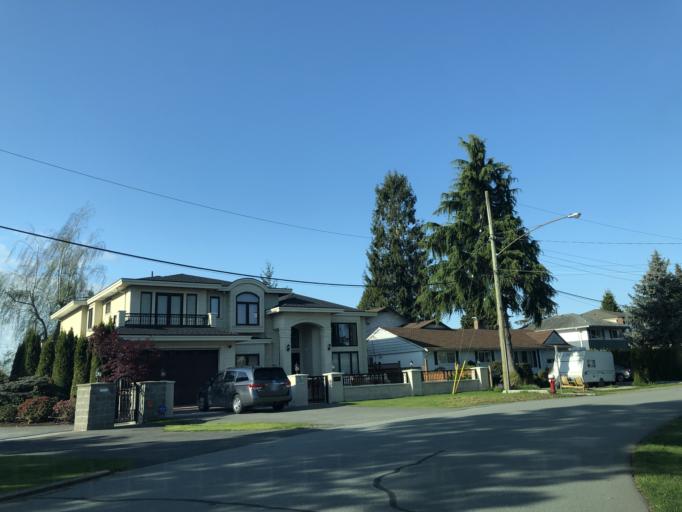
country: CA
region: British Columbia
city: Richmond
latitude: 49.1417
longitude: -123.1155
